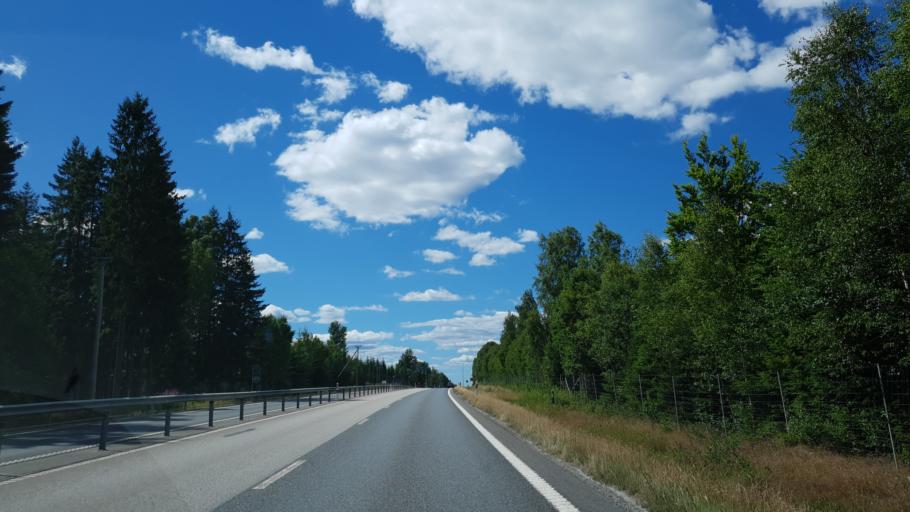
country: SE
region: Kronoberg
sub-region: Vaxjo Kommun
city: Vaexjoe
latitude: 56.8784
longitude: 14.9023
